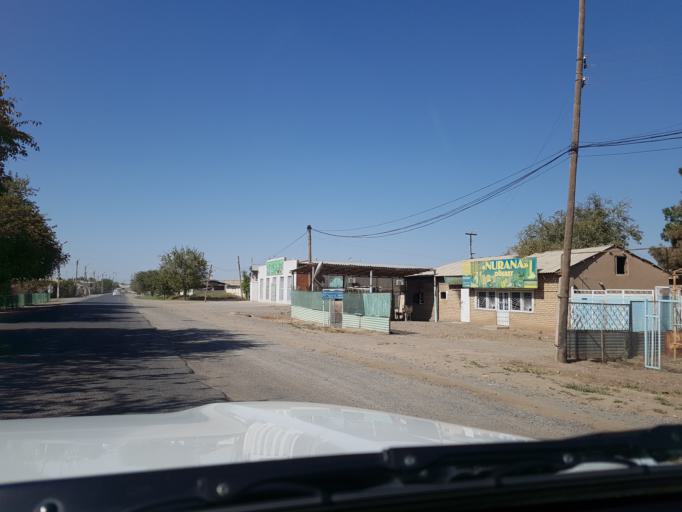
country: IR
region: Razavi Khorasan
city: Sarakhs
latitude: 36.5204
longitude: 61.2186
